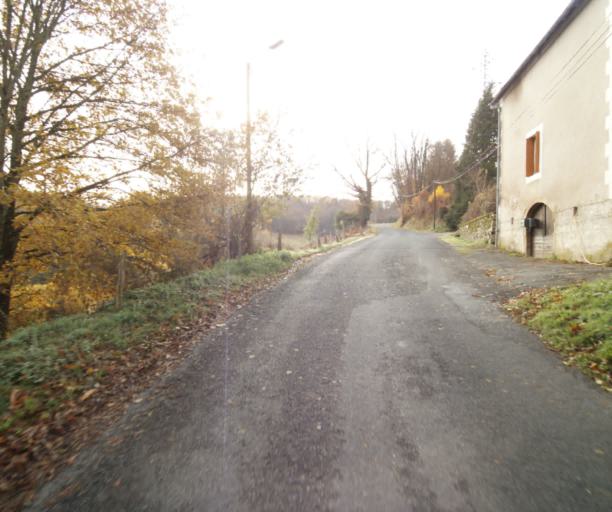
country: FR
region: Limousin
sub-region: Departement de la Correze
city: Cornil
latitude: 45.2179
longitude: 1.7157
